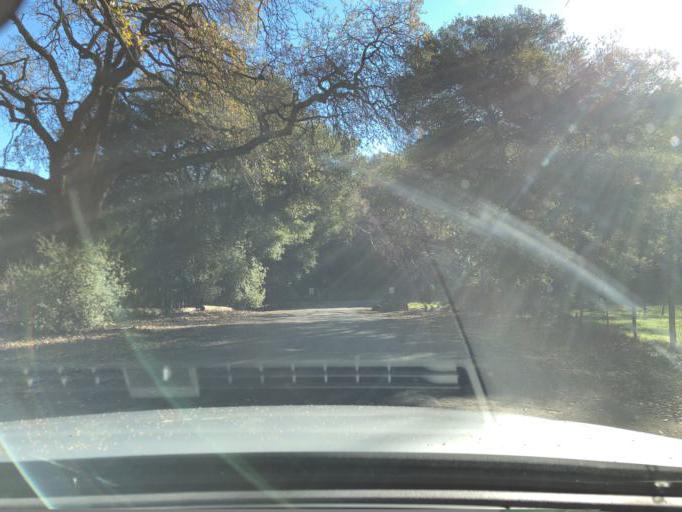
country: US
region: California
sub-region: Santa Clara County
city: Morgan Hill
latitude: 37.1654
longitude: -121.7153
